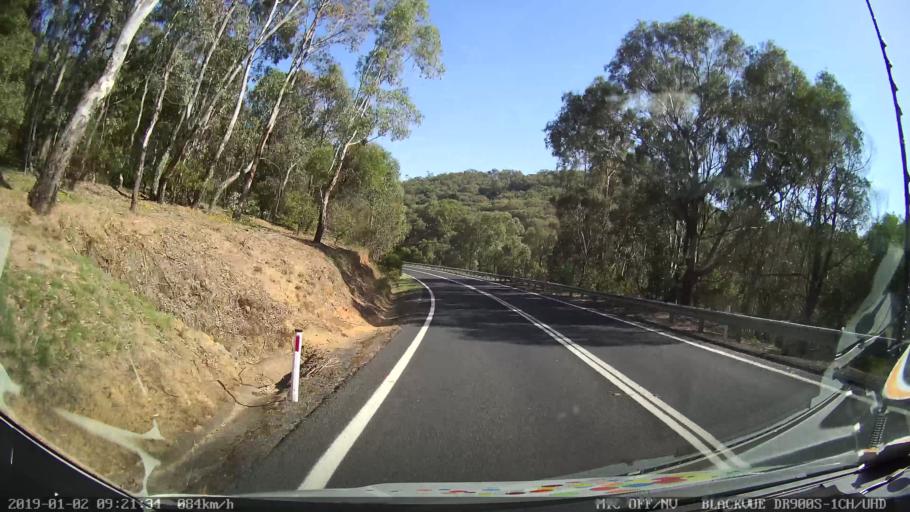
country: AU
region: New South Wales
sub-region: Tumut Shire
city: Tumut
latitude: -35.4042
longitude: 148.2918
